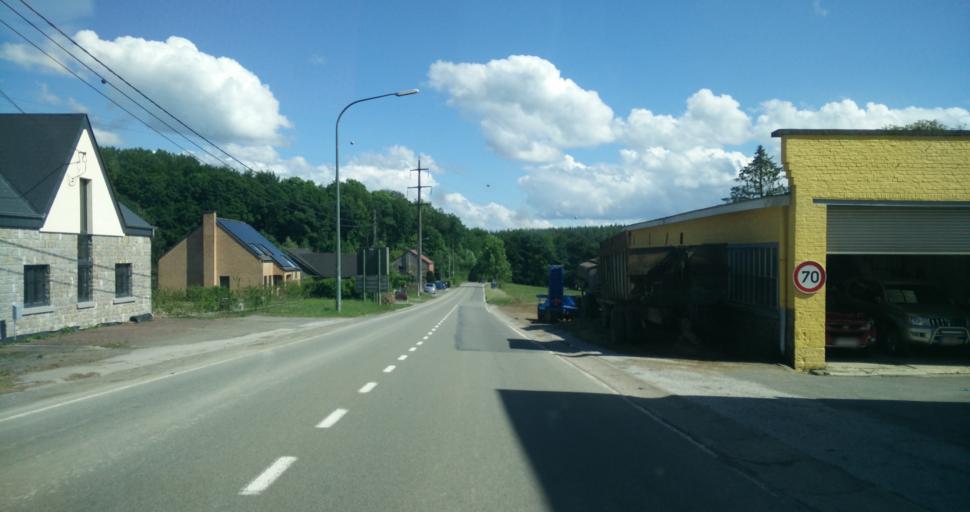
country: BE
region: Wallonia
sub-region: Province du Luxembourg
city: Marche-en-Famenne
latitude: 50.2092
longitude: 5.3683
